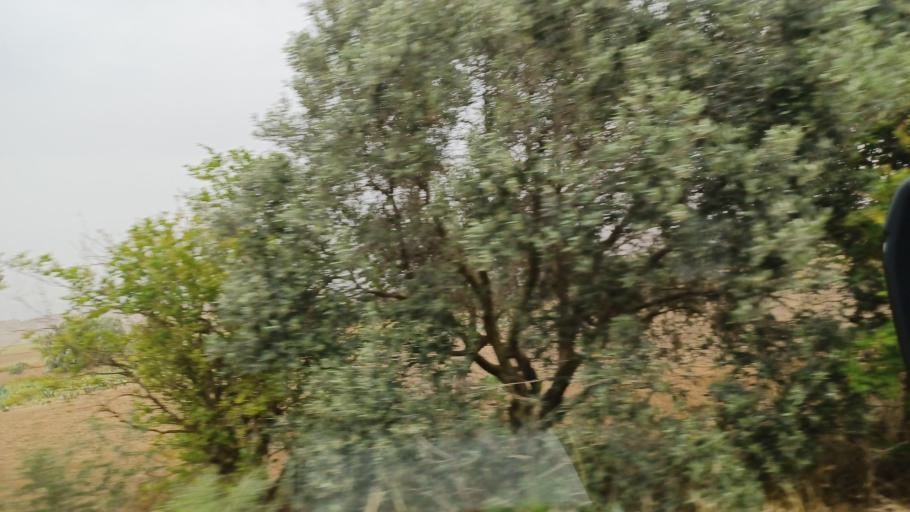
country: CY
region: Lefkosia
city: Mammari
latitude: 35.1847
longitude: 33.1844
